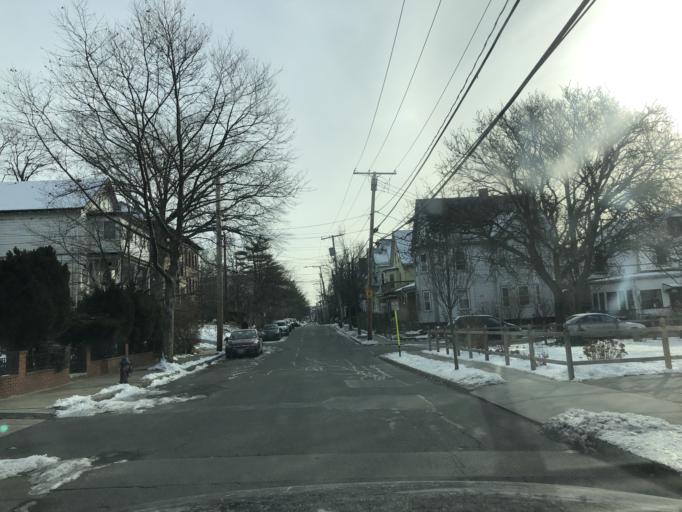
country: US
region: Massachusetts
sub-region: Middlesex County
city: Somerville
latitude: 42.3974
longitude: -71.1200
